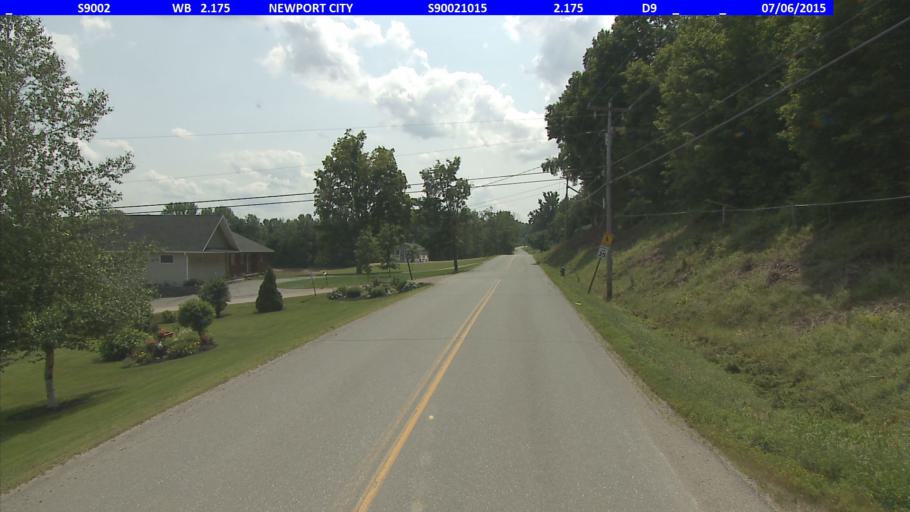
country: US
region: Vermont
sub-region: Orleans County
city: Newport
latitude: 44.9460
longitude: -72.2365
